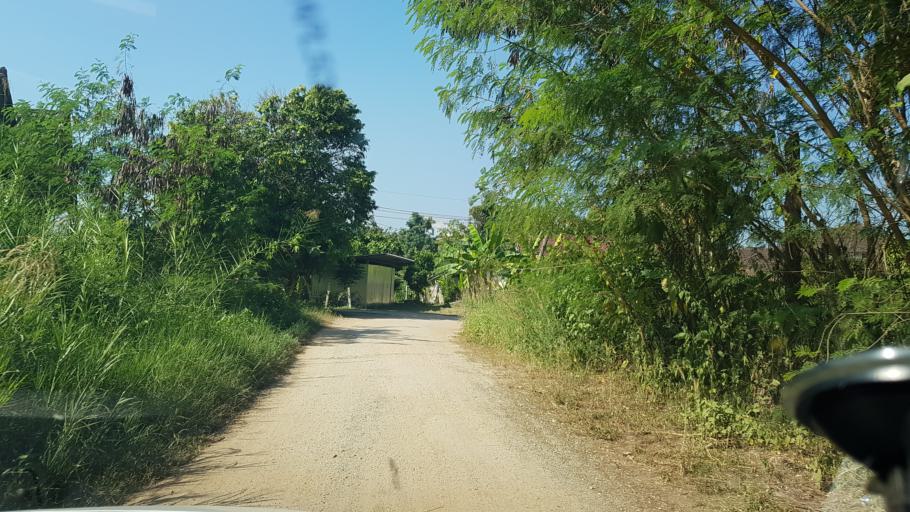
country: TH
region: Chiang Rai
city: Chiang Rai
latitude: 19.9020
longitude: 99.7941
